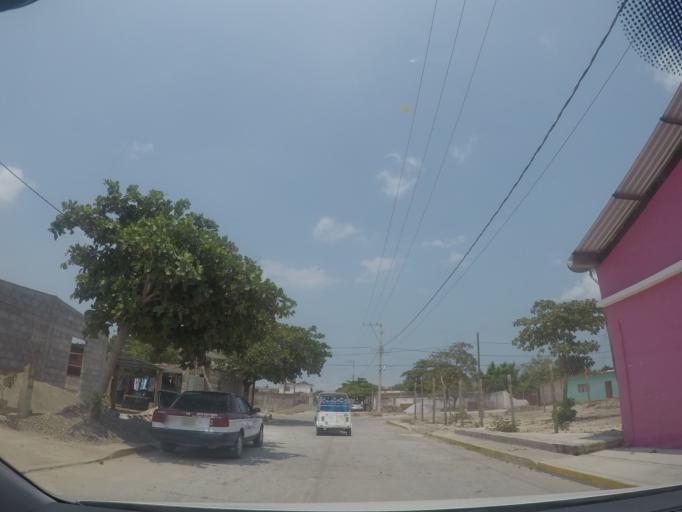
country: MX
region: Oaxaca
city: Asuncion Ixtaltepec
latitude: 16.5034
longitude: -95.0617
